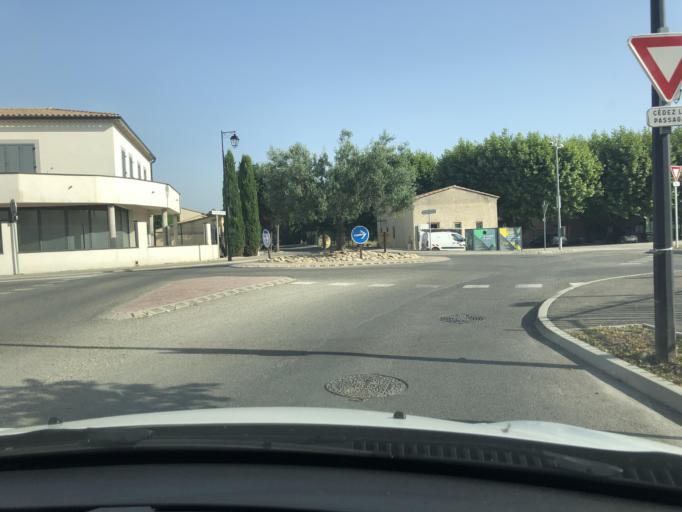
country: FR
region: Provence-Alpes-Cote d'Azur
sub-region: Departement du Vaucluse
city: Velleron
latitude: 43.9592
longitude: 5.0322
